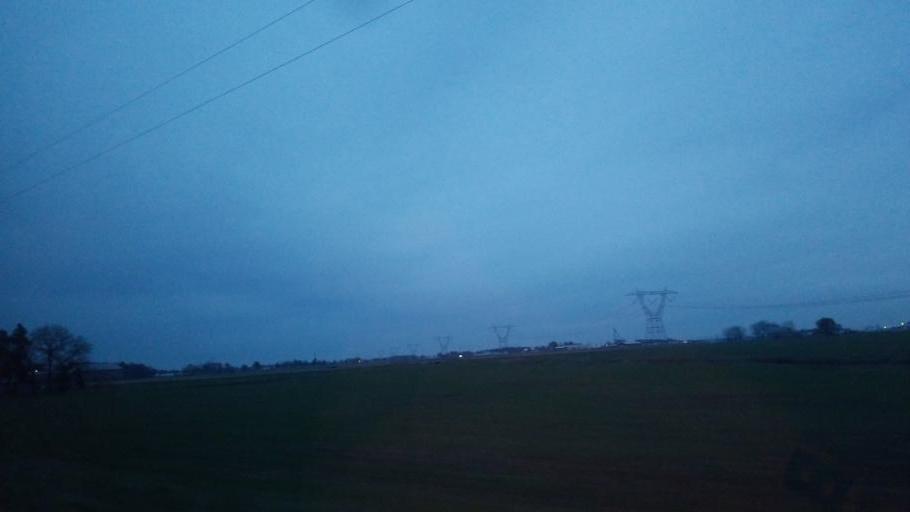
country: US
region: Indiana
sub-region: Adams County
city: Berne
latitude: 40.7157
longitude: -84.9782
